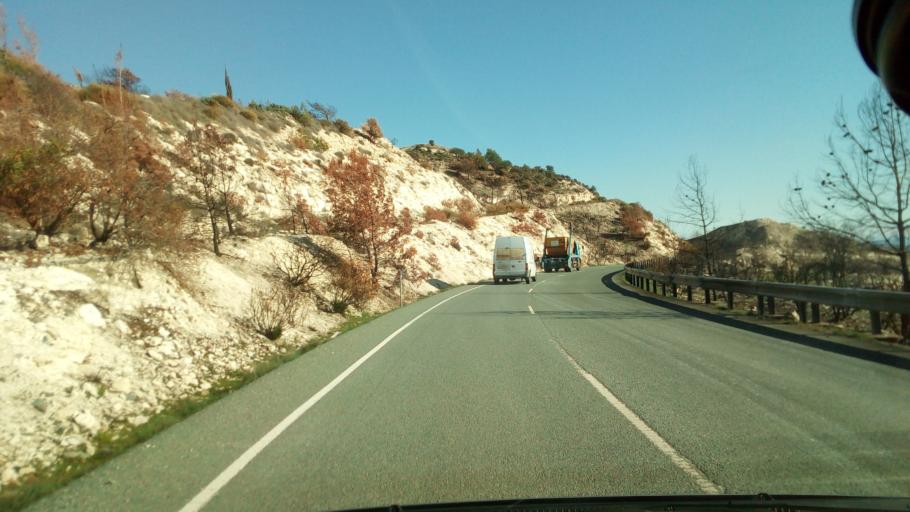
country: CY
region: Larnaka
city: Kofinou
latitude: 34.8146
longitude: 33.3082
